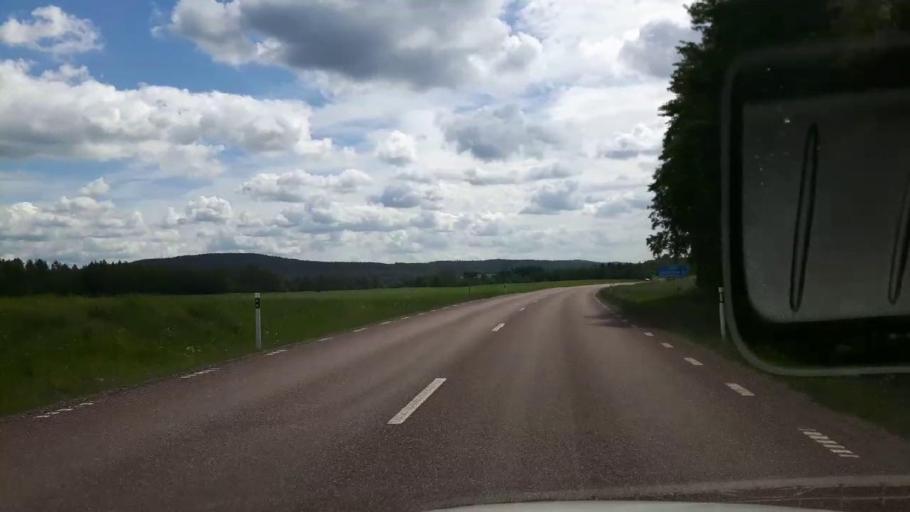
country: SE
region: Dalarna
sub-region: Hedemora Kommun
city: Langshyttan
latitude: 60.3891
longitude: 15.9019
